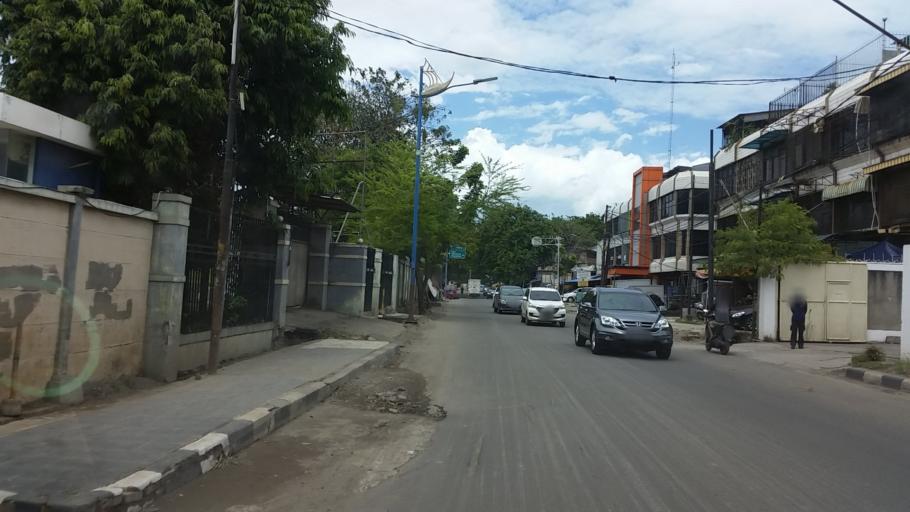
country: ID
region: Jakarta Raya
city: Jakarta
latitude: -6.1287
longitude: 106.8112
